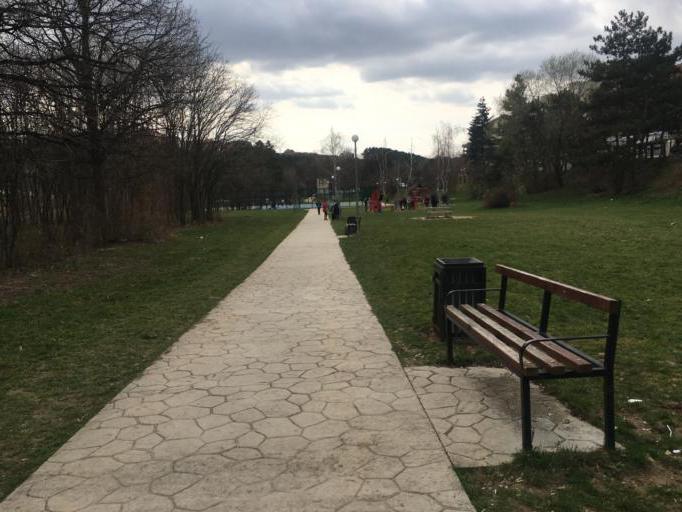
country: XK
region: Pristina
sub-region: Komuna e Prishtines
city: Pristina
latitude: 42.6666
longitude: 21.1860
